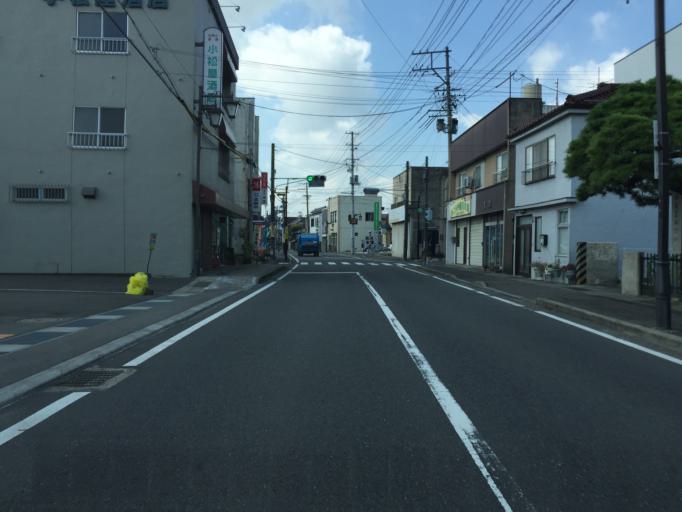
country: JP
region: Fukushima
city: Motomiya
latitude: 37.5198
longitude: 140.4054
